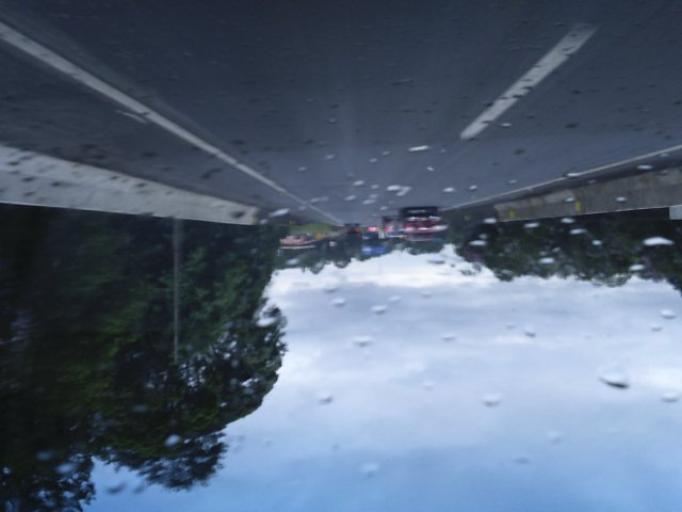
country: BR
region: Parana
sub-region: Guaratuba
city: Guaratuba
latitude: -25.9778
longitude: -48.8885
